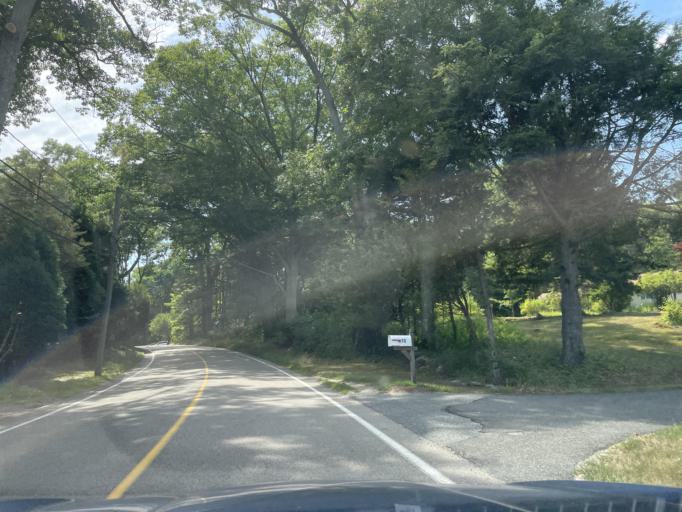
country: US
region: Massachusetts
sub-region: Middlesex County
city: Sherborn
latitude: 42.2409
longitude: -71.3840
